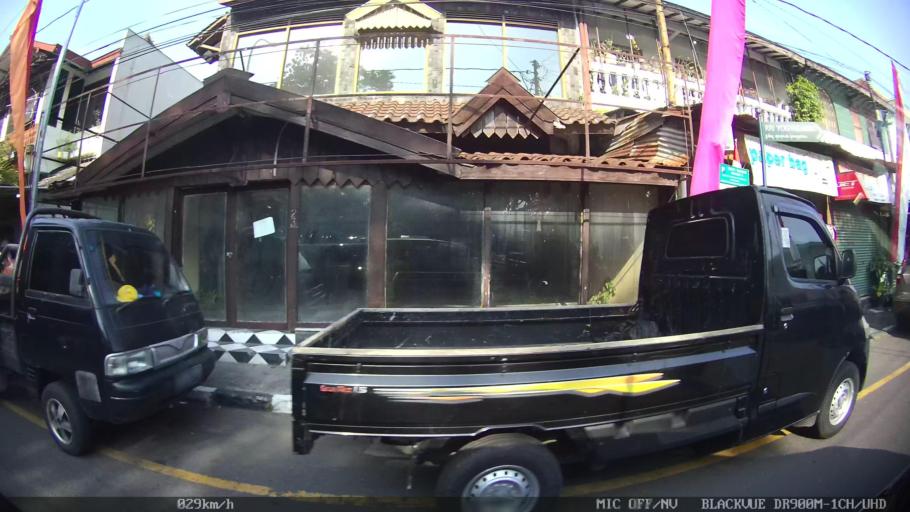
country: ID
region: Daerah Istimewa Yogyakarta
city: Yogyakarta
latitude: -7.7886
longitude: 110.3689
